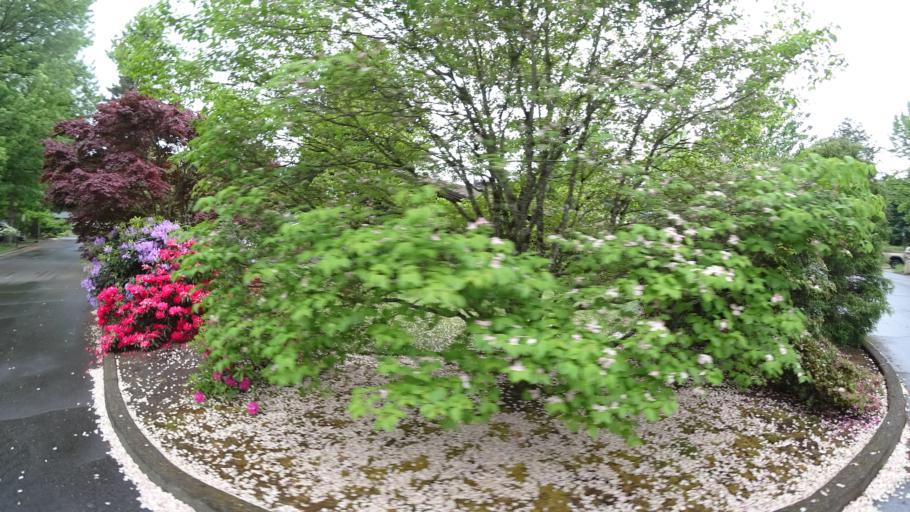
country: US
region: Oregon
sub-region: Washington County
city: Raleigh Hills
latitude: 45.4722
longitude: -122.7687
